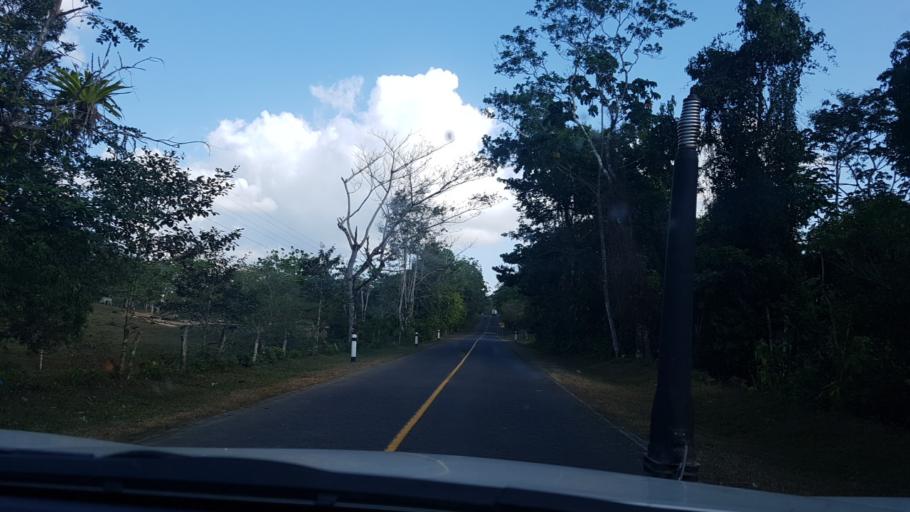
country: NI
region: Atlantico Sur
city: Nueva Guinea
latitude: 11.6954
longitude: -84.4062
